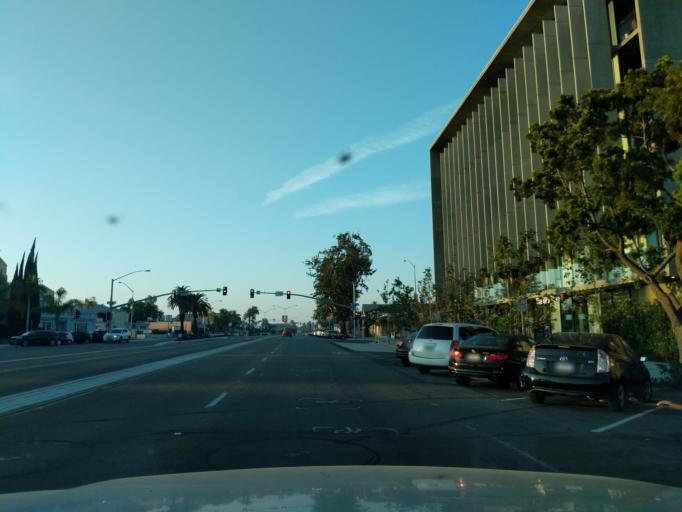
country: US
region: California
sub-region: San Diego County
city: San Diego
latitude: 32.7515
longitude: -117.1463
